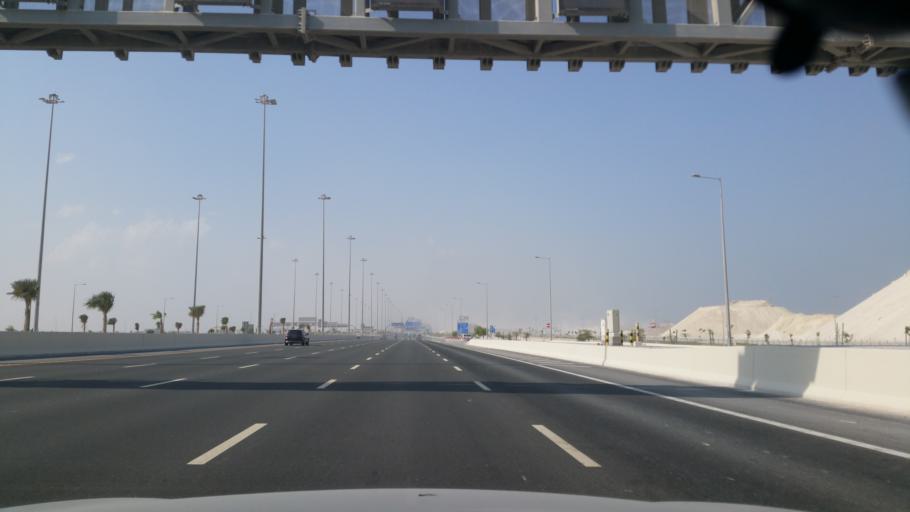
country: QA
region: Baladiyat Umm Salal
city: Umm Salal Muhammad
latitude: 25.4351
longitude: 51.4834
